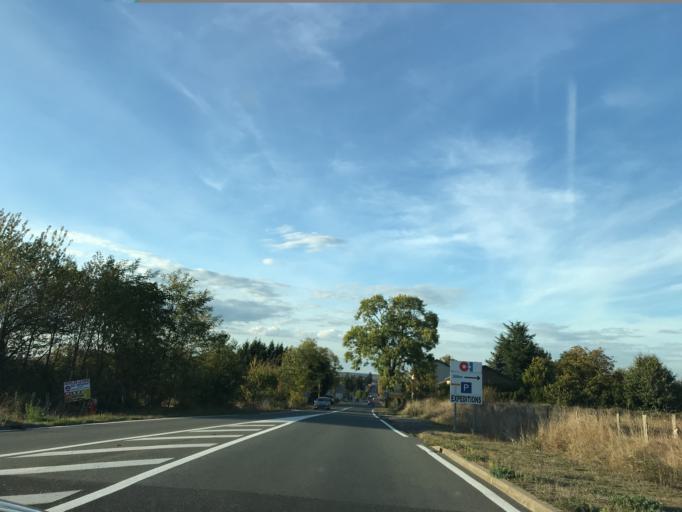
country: FR
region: Auvergne
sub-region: Departement du Puy-de-Dome
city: Puy-Guillaume
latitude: 45.9478
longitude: 3.4824
